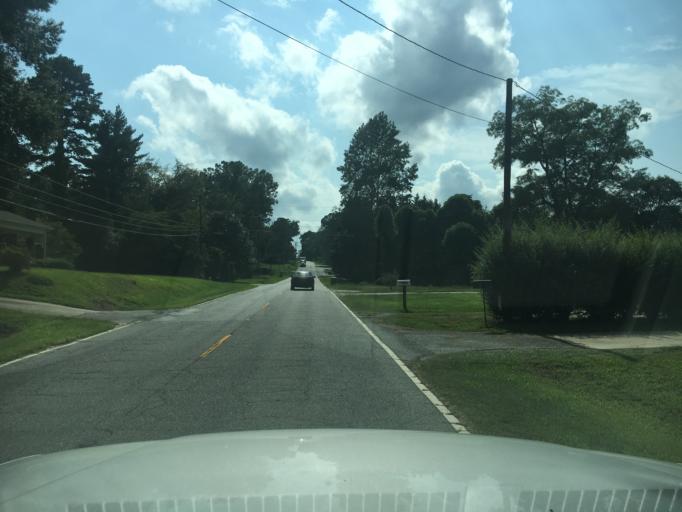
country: US
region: South Carolina
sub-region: Anderson County
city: Belton
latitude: 34.5277
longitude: -82.4833
